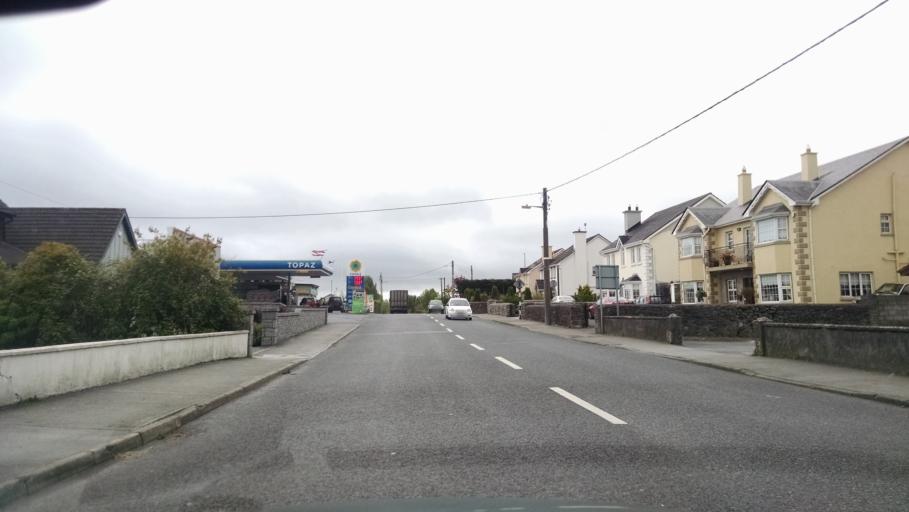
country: IE
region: Connaught
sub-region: County Galway
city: Moycullen
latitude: 53.4688
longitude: -9.1068
